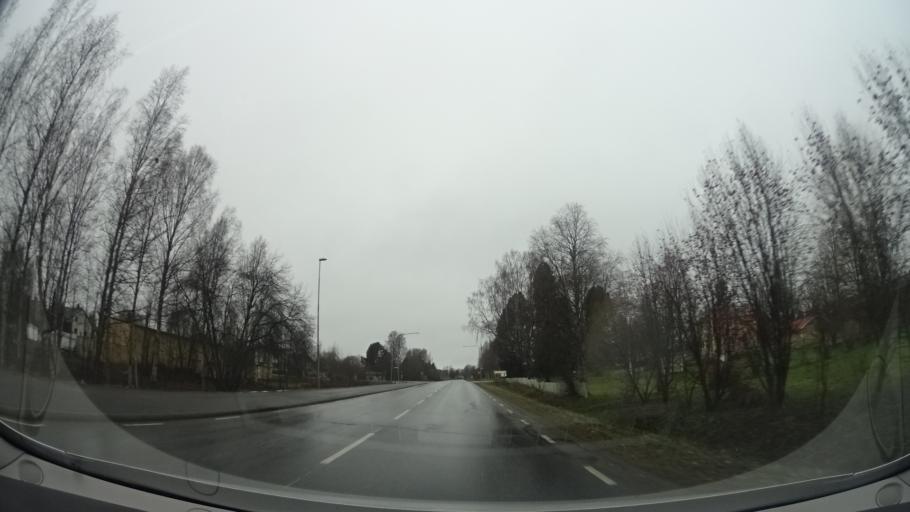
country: SE
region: Vaesterbotten
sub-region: Skelleftea Kommun
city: Kage
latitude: 64.8383
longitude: 20.9871
